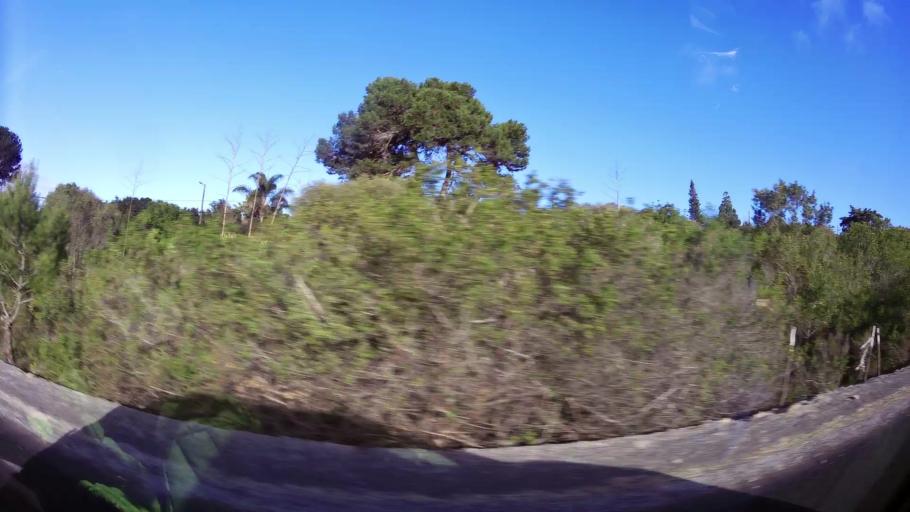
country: ZA
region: Western Cape
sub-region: Eden District Municipality
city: George
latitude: -33.9950
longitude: 22.6167
